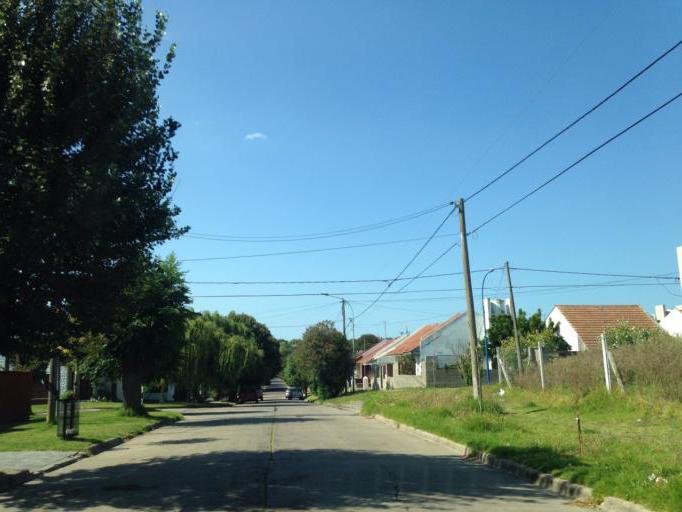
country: AR
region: Buenos Aires
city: Mar del Plata
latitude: -38.0337
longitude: -57.5491
